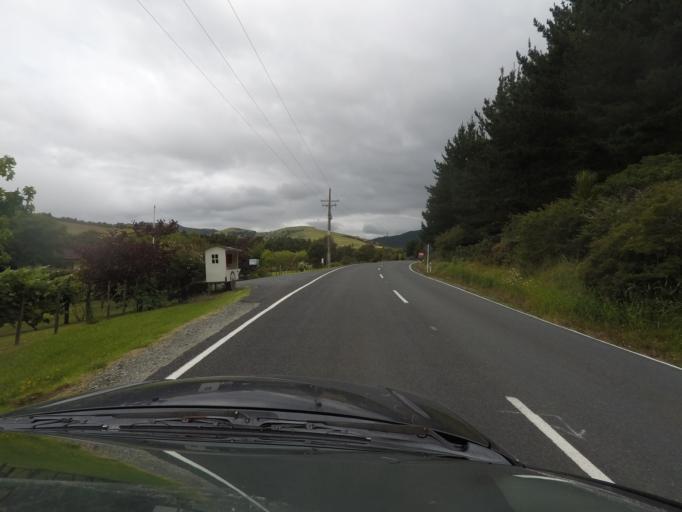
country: NZ
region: Auckland
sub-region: Auckland
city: Wellsford
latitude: -36.2882
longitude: 174.6131
